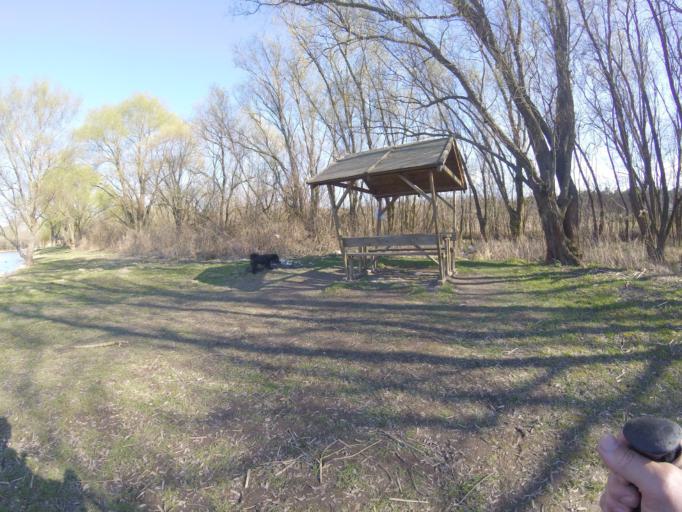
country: HU
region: Komarom-Esztergom
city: Bokod
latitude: 47.4823
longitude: 18.2709
